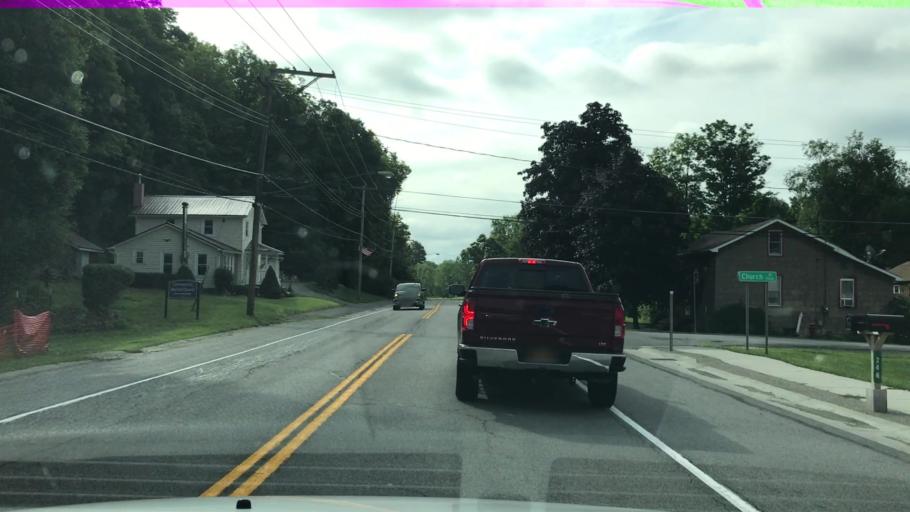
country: US
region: New York
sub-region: Erie County
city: Alden
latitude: 42.8429
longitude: -78.4681
